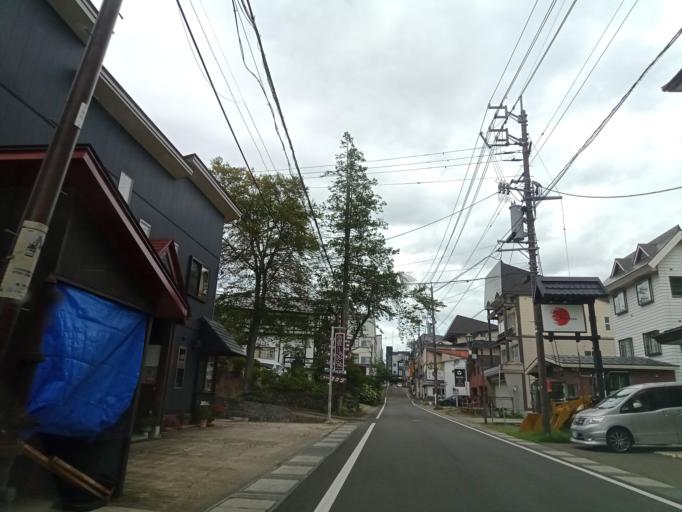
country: JP
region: Niigata
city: Arai
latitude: 36.8924
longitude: 138.1774
